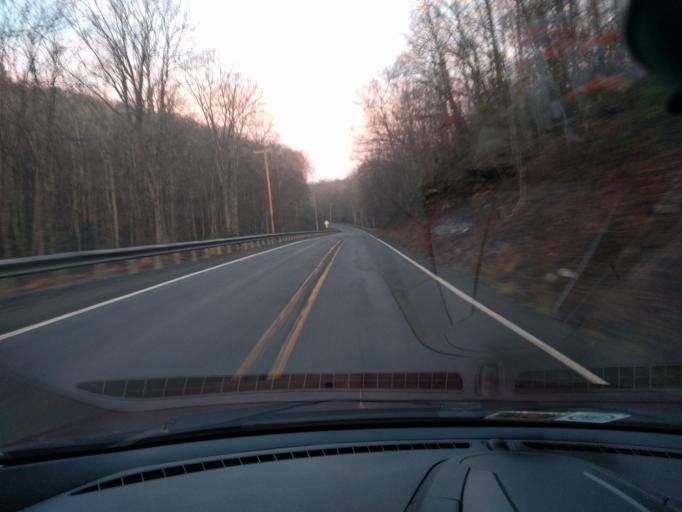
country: US
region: West Virginia
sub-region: Fayette County
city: Fayetteville
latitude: 38.0481
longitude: -80.9407
